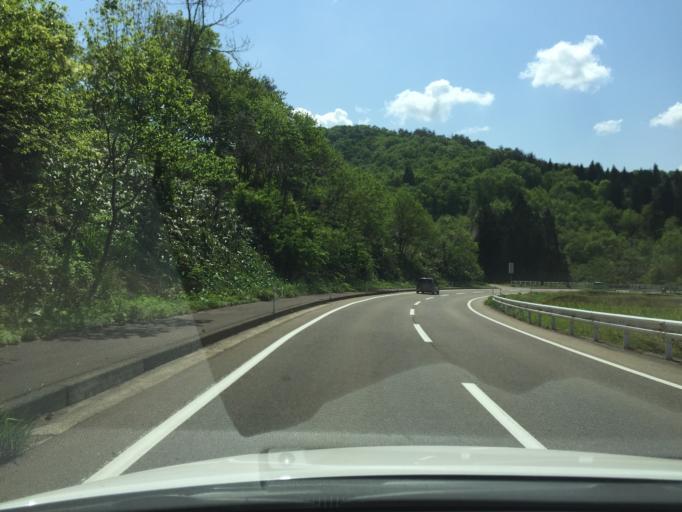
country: JP
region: Niigata
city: Kamo
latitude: 37.5909
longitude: 139.0939
